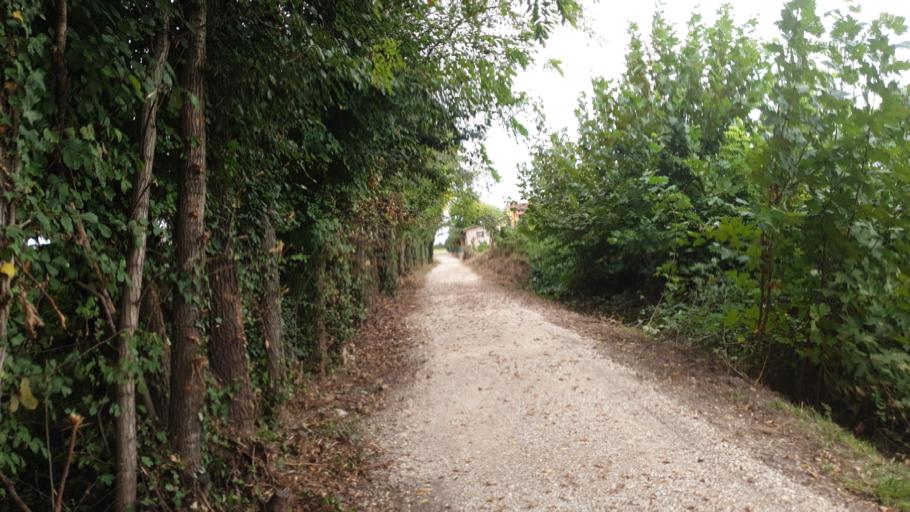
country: IT
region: Veneto
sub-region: Provincia di Padova
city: Albignasego
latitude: 45.3510
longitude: 11.9025
